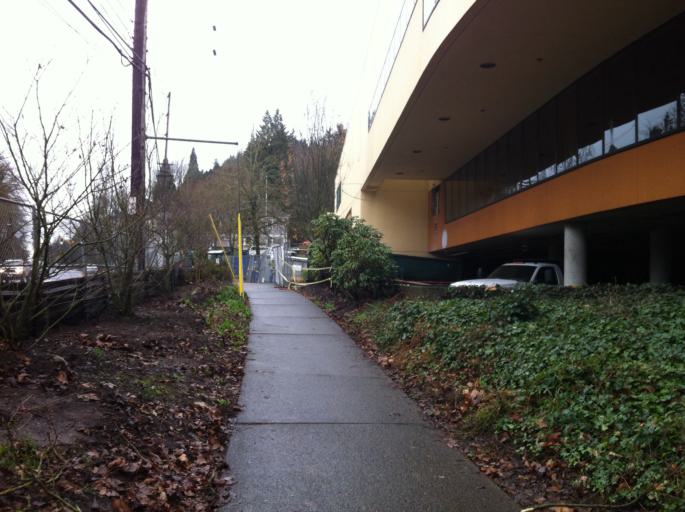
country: US
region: Oregon
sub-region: Multnomah County
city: Portland
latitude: 45.5034
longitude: -122.6822
